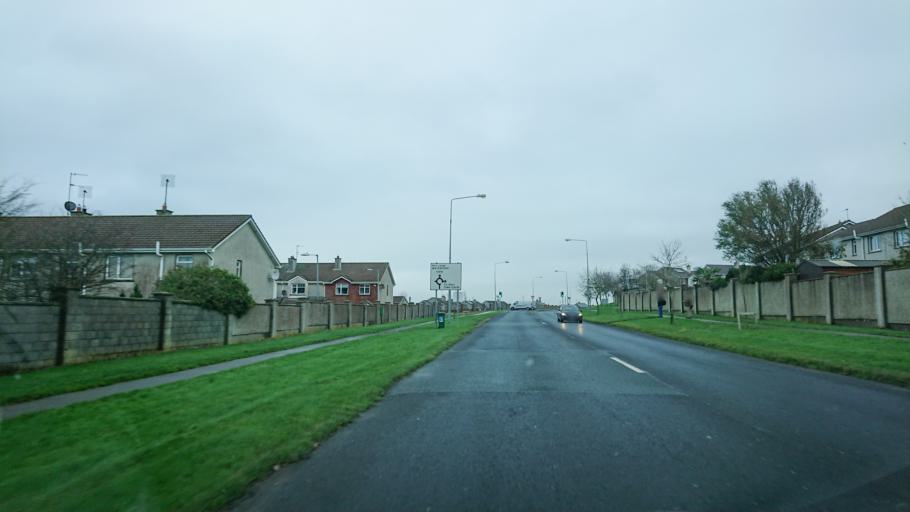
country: IE
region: Munster
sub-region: Waterford
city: Tra Mhor
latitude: 52.1649
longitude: -7.1648
